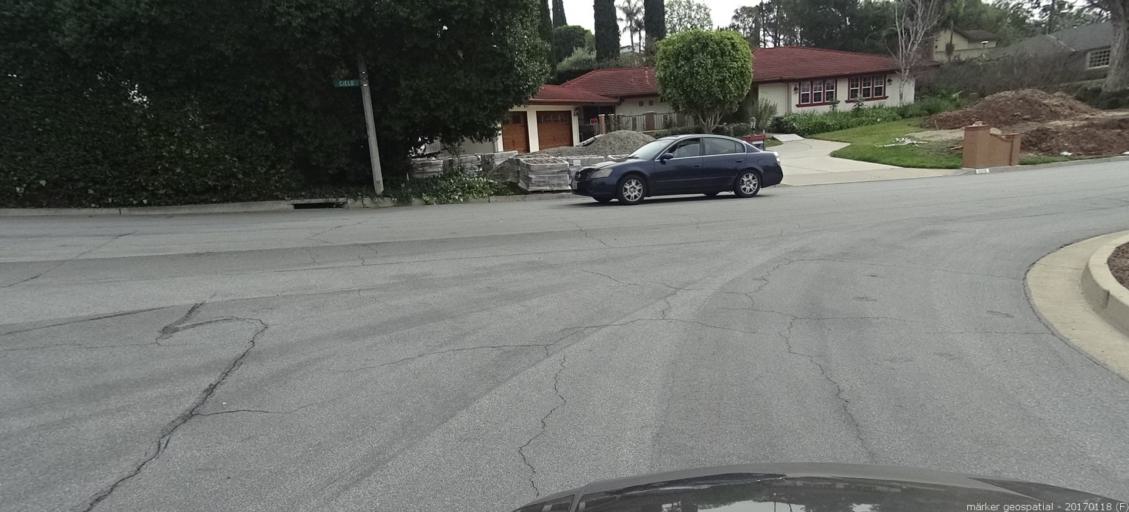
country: US
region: California
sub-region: Orange County
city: North Tustin
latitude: 33.7646
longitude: -117.7888
